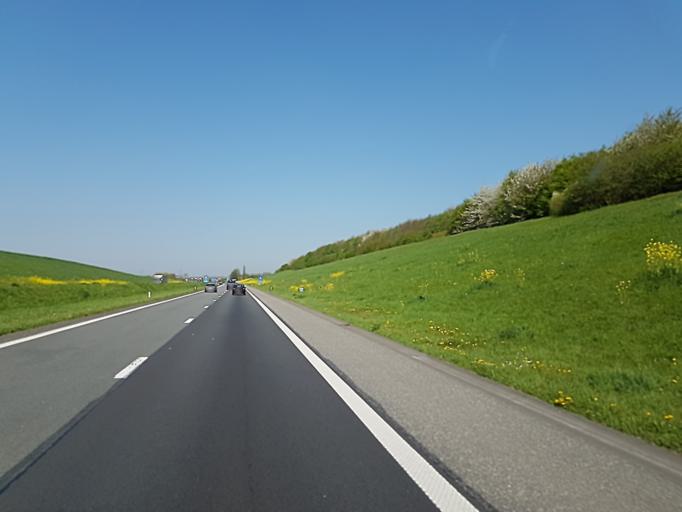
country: BE
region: Flanders
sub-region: Provincie West-Vlaanderen
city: Zonnebeke
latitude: 50.8508
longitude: 2.9782
